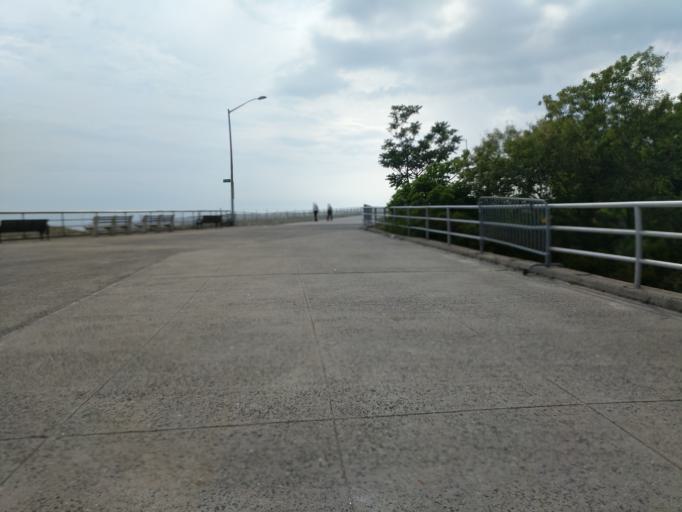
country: US
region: New York
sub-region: Nassau County
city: Atlantic Beach
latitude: 40.5926
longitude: -73.7539
